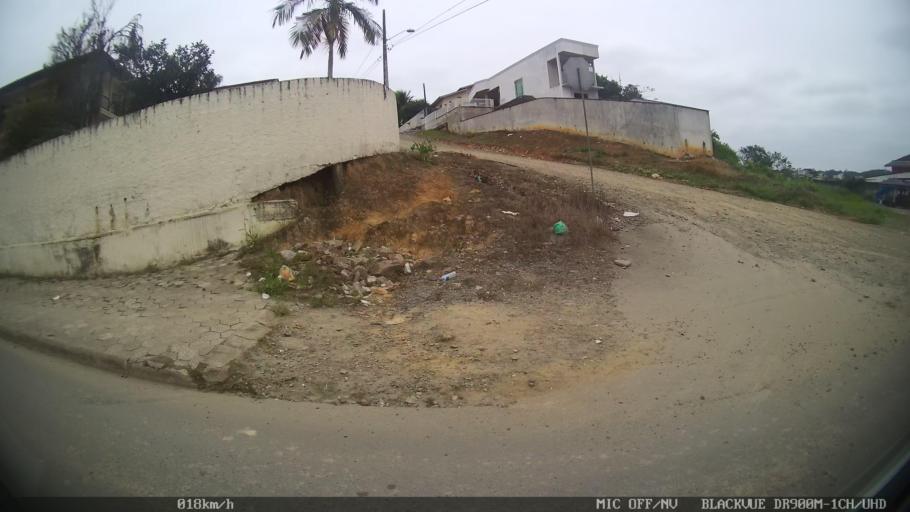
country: BR
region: Santa Catarina
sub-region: Joinville
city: Joinville
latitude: -26.3609
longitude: -48.8262
